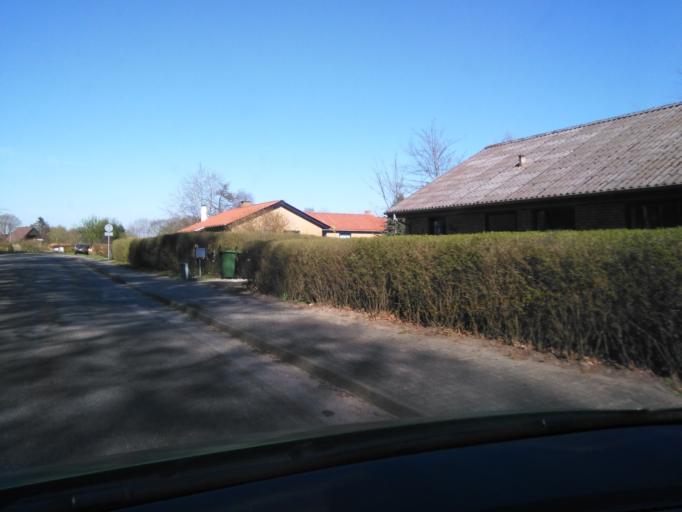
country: DK
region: South Denmark
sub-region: Varde Kommune
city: Oksbol
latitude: 55.6515
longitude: 8.2888
